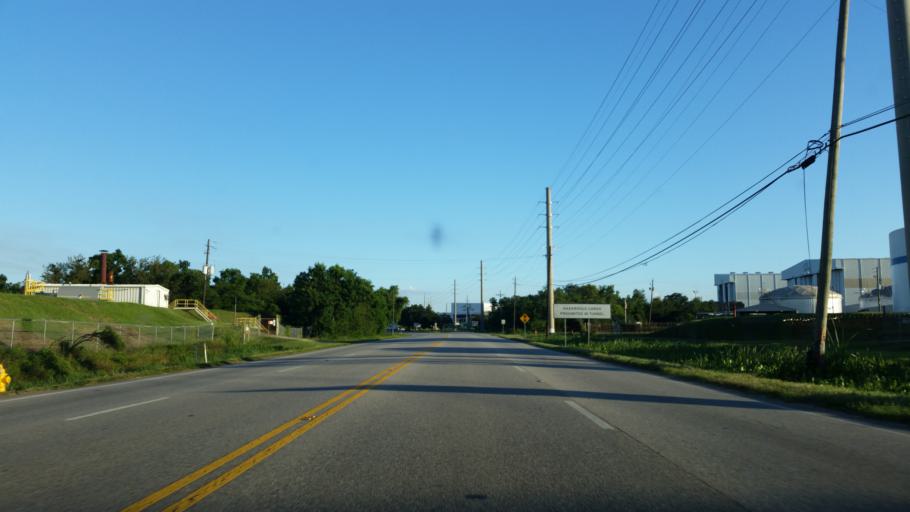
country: US
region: Alabama
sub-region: Mobile County
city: Mobile
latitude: 30.6970
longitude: -88.0318
